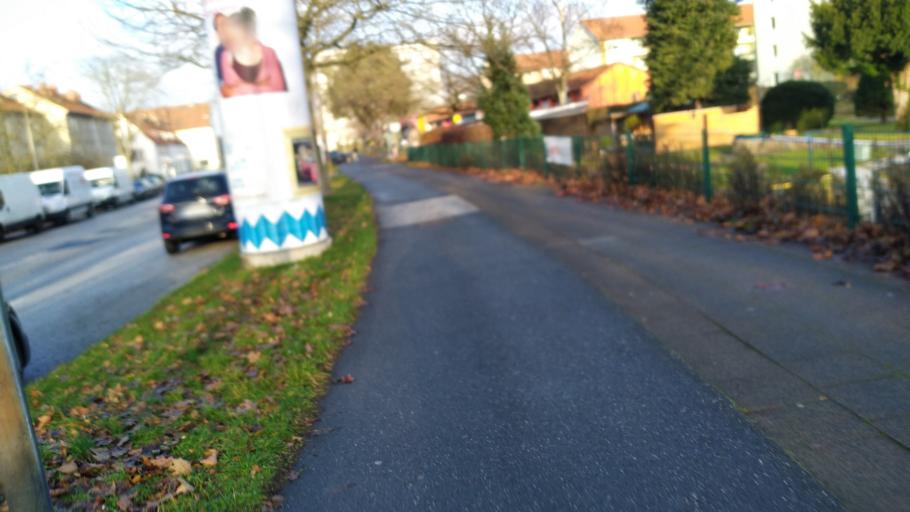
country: DE
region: Mecklenburg-Vorpommern
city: Selmsdorf
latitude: 53.9159
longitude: 10.8131
